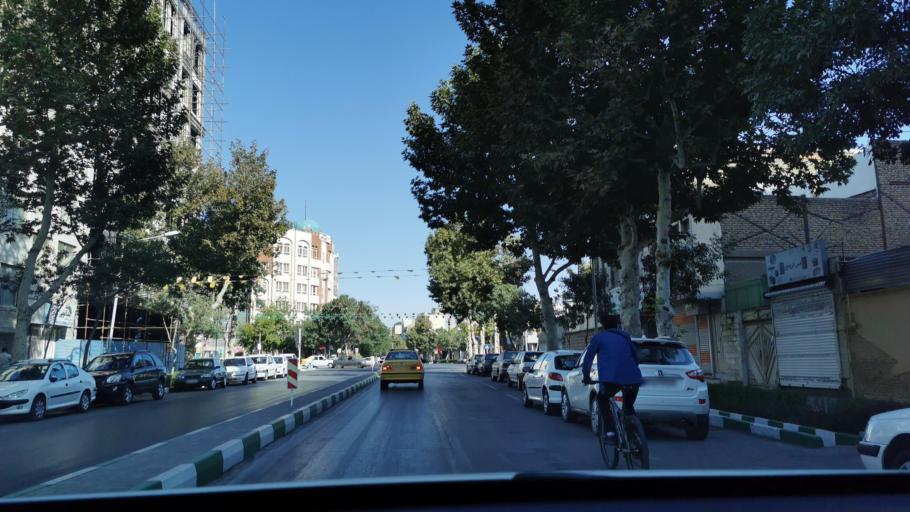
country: IR
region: Razavi Khorasan
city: Mashhad
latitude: 36.2992
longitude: 59.6186
